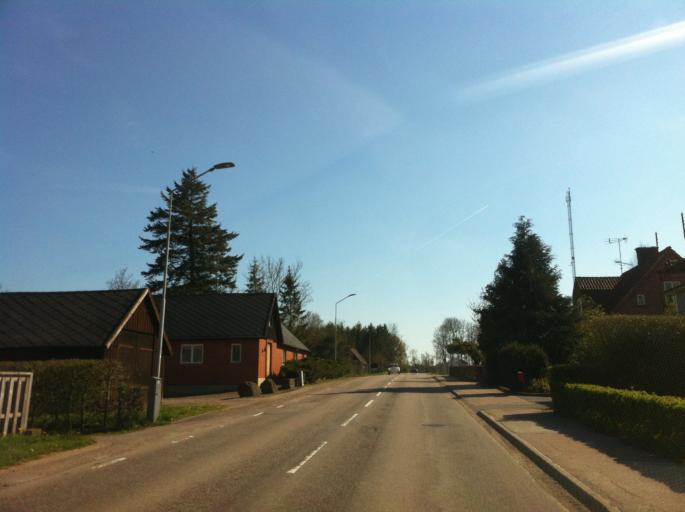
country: SE
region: Skane
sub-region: Svalovs Kommun
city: Kagerod
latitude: 56.0302
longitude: 13.1067
